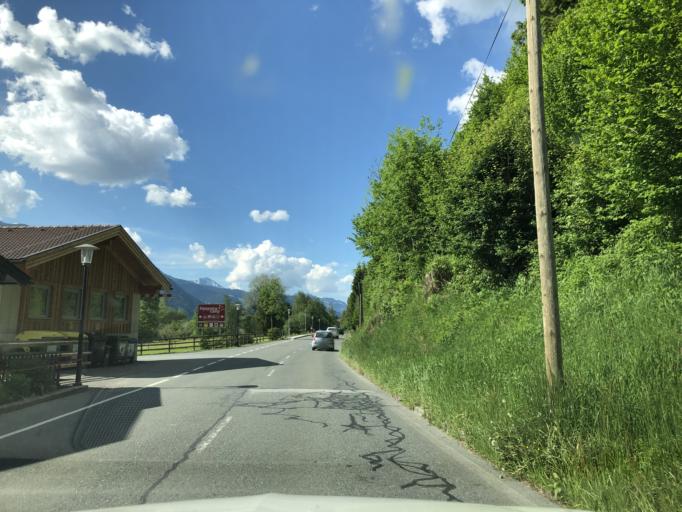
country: AT
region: Salzburg
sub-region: Politischer Bezirk Zell am See
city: Bruck an der Grossglocknerstrasse
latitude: 47.3017
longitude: 12.8162
